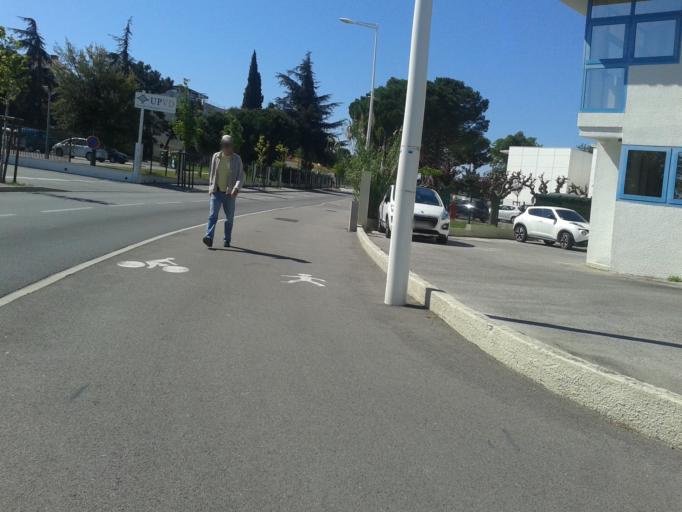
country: FR
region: Languedoc-Roussillon
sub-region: Departement des Pyrenees-Orientales
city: Perpignan
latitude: 42.6850
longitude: 2.8987
